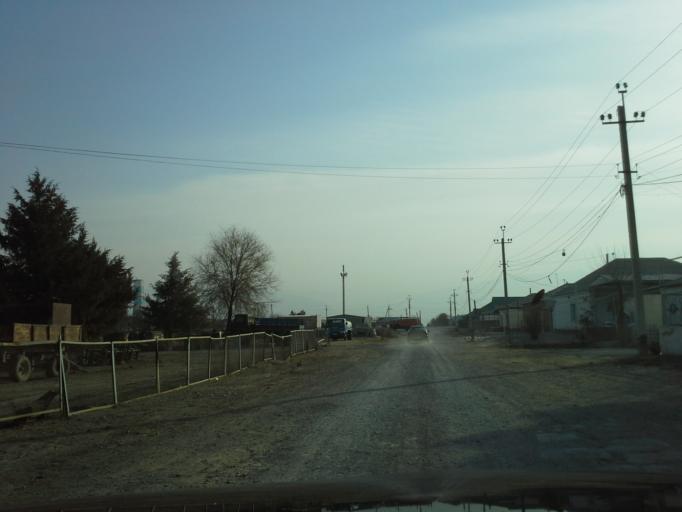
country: TM
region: Ahal
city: Abadan
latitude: 38.1752
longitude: 58.0452
